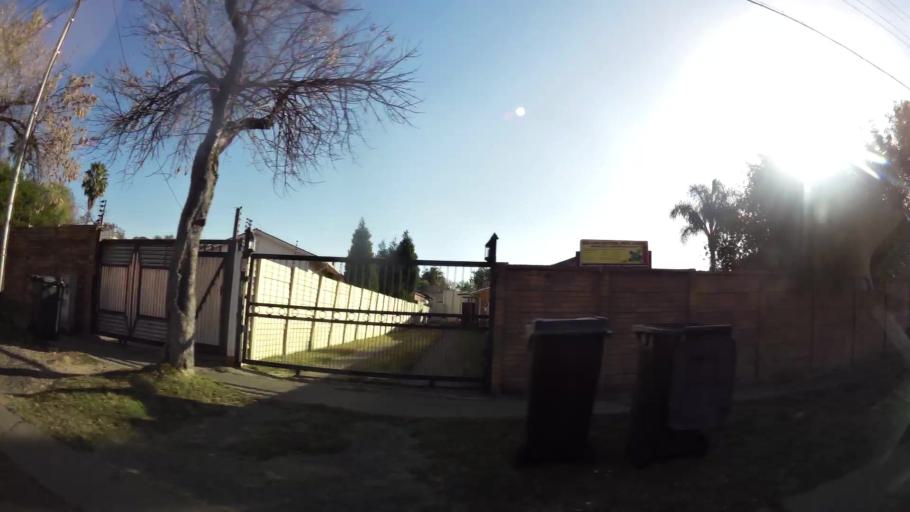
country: ZA
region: Gauteng
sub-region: City of Tshwane Metropolitan Municipality
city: Pretoria
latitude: -25.7236
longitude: 28.2107
